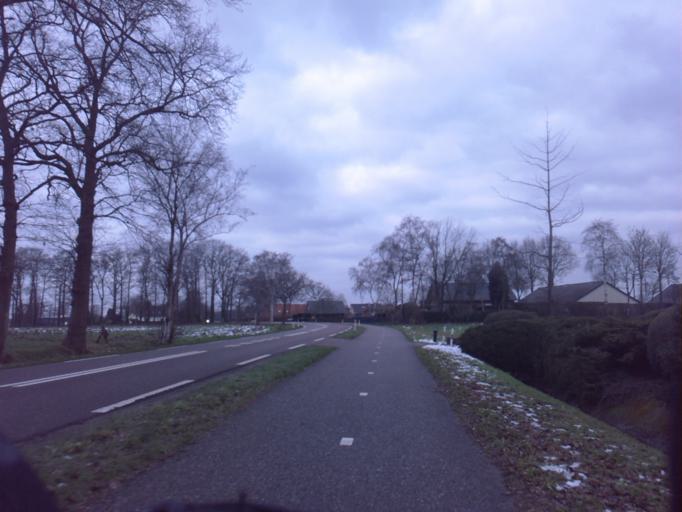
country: NL
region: Gelderland
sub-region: Gemeente Barneveld
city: Terschuur
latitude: 52.1412
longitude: 5.4831
